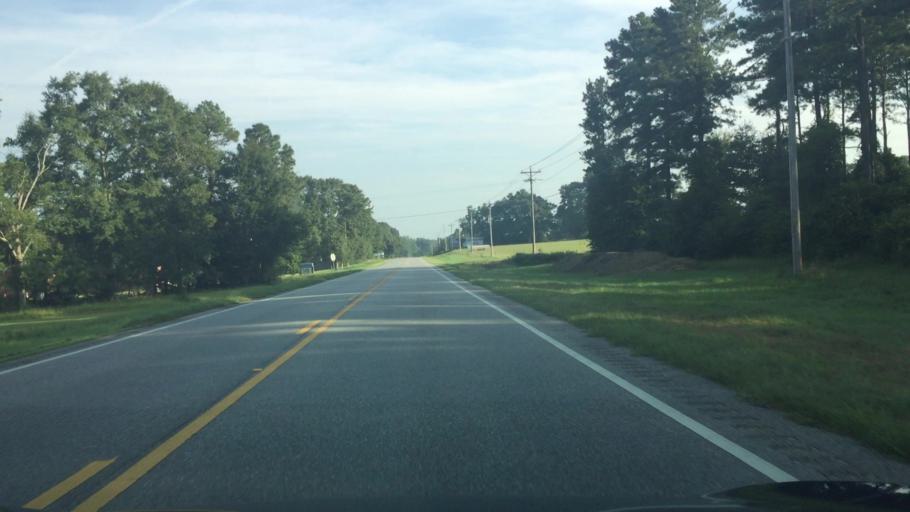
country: US
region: Alabama
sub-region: Covington County
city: Andalusia
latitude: 31.2626
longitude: -86.4714
